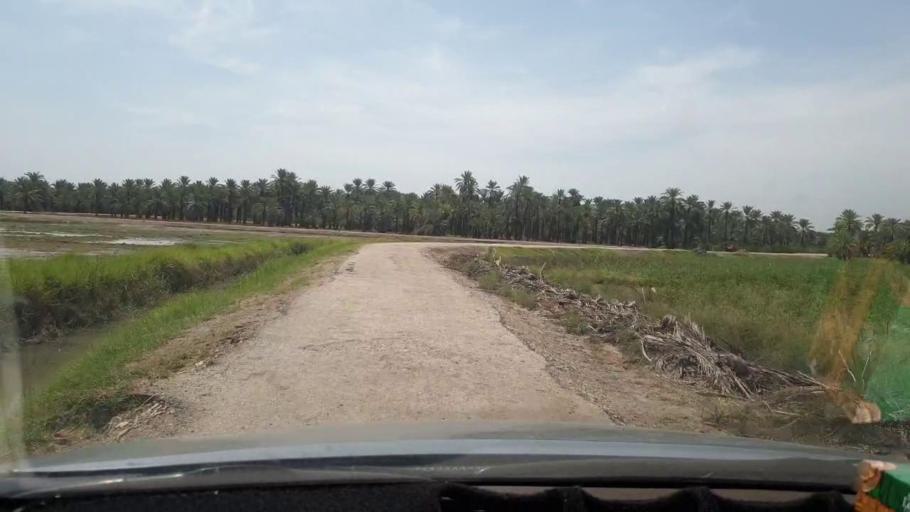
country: PK
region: Sindh
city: Khairpur
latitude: 27.4841
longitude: 68.7728
